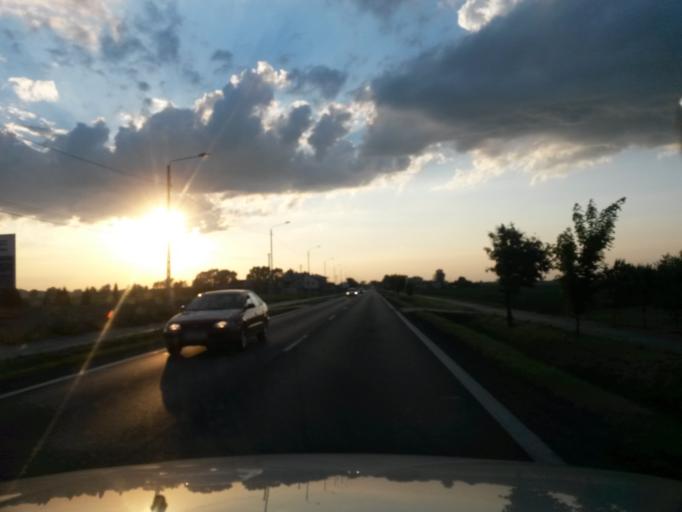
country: PL
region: Lodz Voivodeship
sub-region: Powiat wielunski
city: Wielun
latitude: 51.2397
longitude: 18.5300
